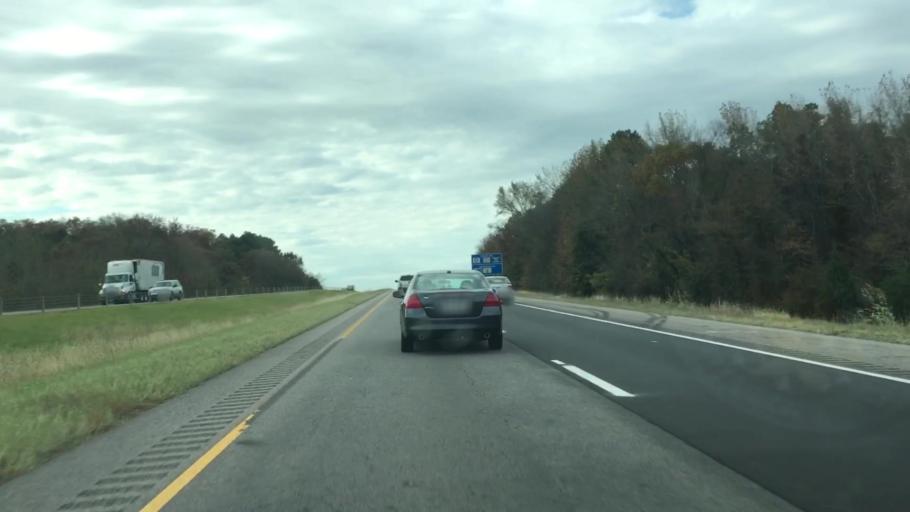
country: US
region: Arkansas
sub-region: Conway County
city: Morrilton
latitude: 35.1694
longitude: -92.6920
